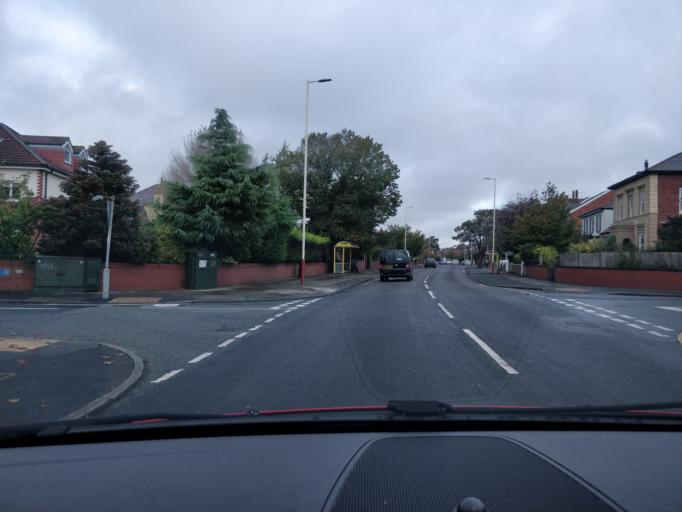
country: GB
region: England
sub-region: Sefton
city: Southport
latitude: 53.6243
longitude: -3.0129
